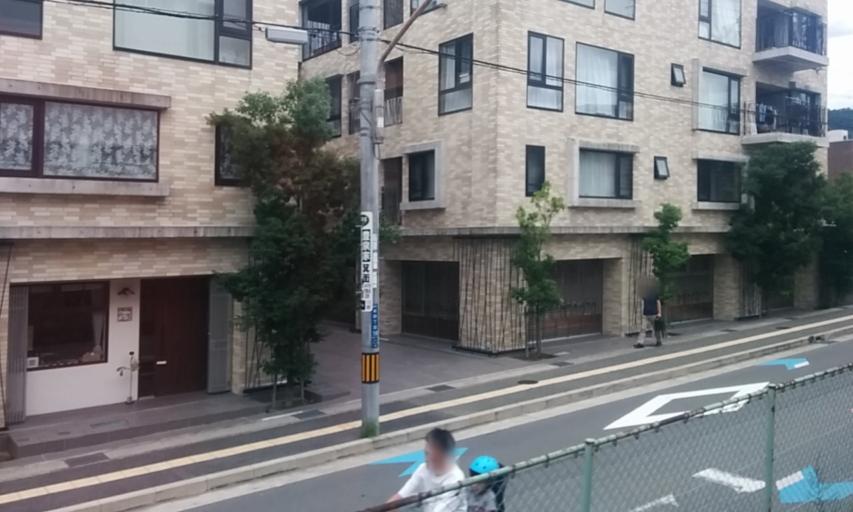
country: JP
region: Osaka
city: Mino
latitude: 34.8247
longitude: 135.4661
